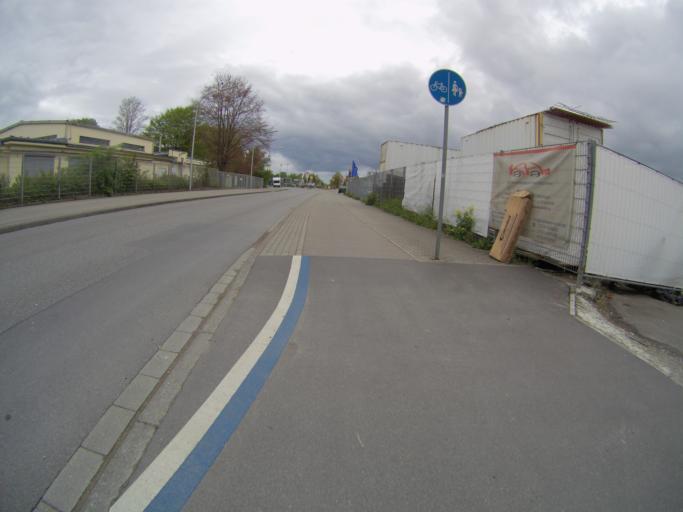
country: DE
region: Baden-Wuerttemberg
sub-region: Freiburg Region
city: Konstanz
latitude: 47.6760
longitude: 9.1616
